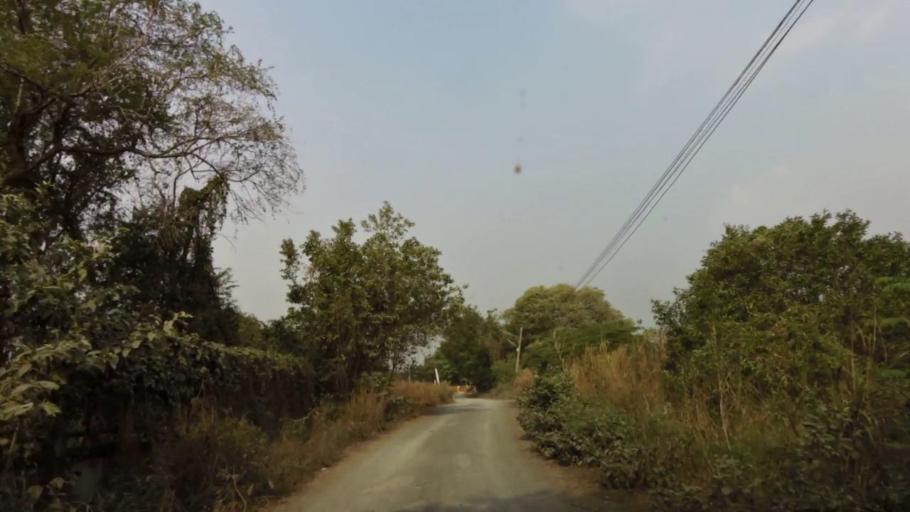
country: TH
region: Phra Nakhon Si Ayutthaya
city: Phra Nakhon Si Ayutthaya
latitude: 14.3370
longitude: 100.5804
